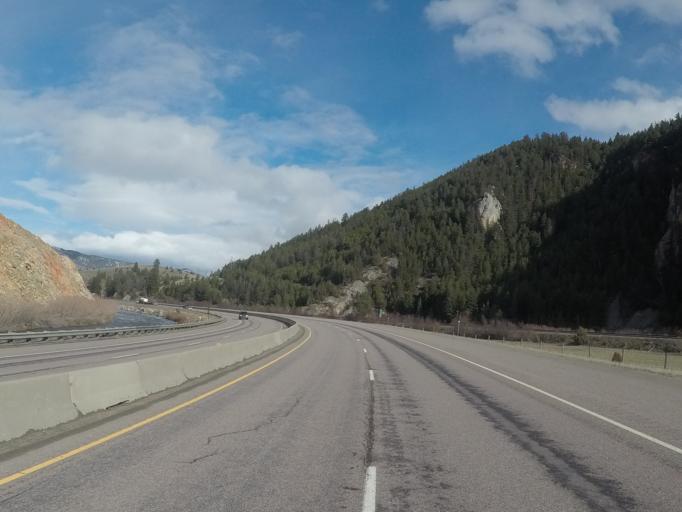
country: US
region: Montana
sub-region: Granite County
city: Philipsburg
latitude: 46.7163
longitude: -113.3085
